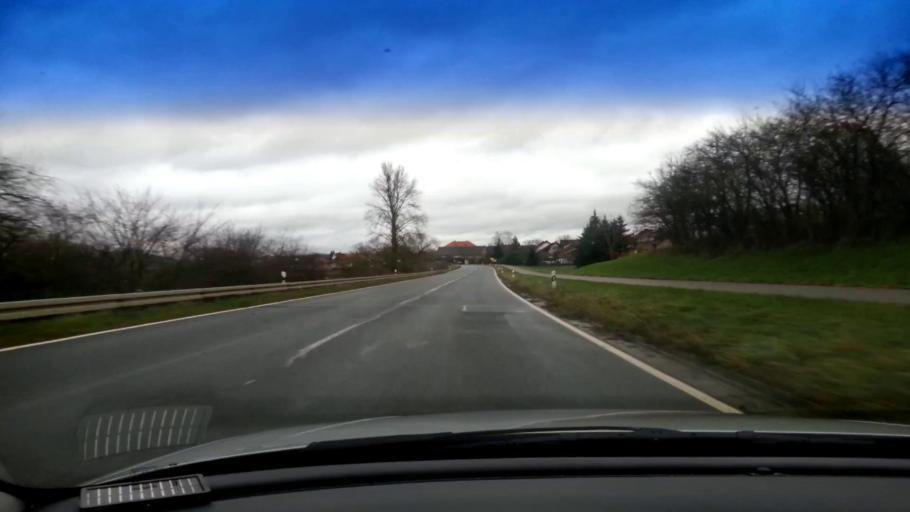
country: DE
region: Bavaria
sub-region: Upper Franconia
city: Zapfendorf
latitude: 50.0337
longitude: 10.9421
